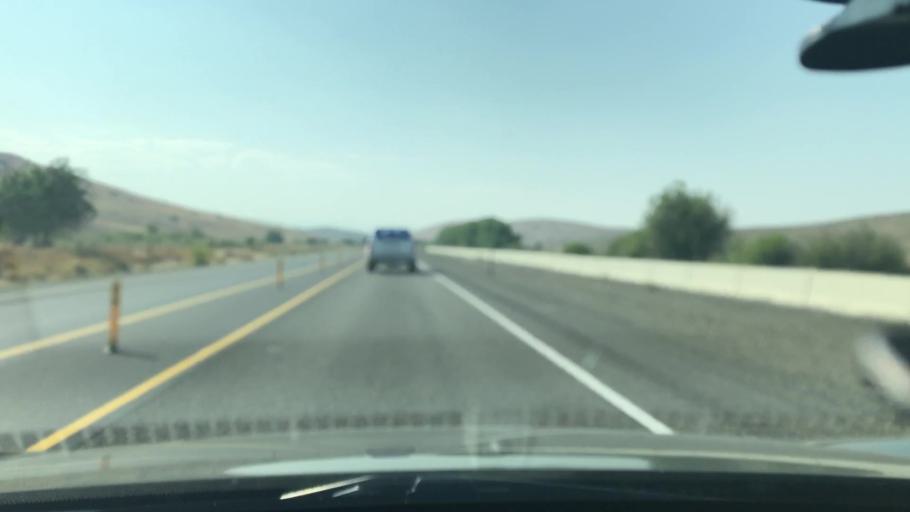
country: US
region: Oregon
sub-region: Baker County
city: Baker City
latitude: 44.6752
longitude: -117.6382
